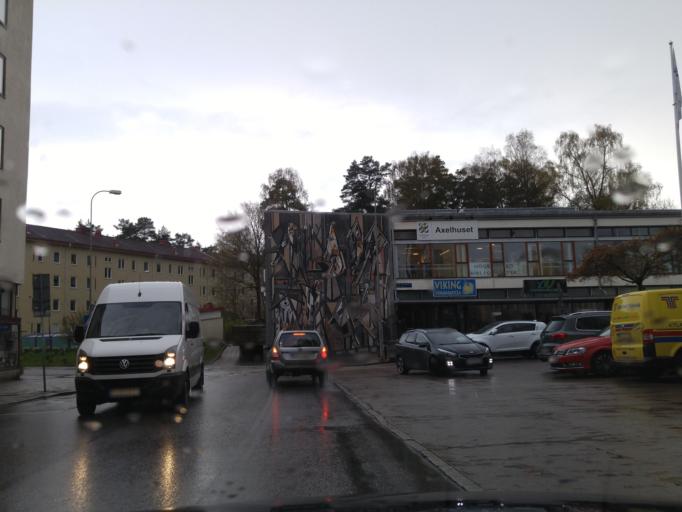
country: SE
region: Vaestra Goetaland
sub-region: Goteborg
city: Majorna
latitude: 57.6710
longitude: 11.9278
